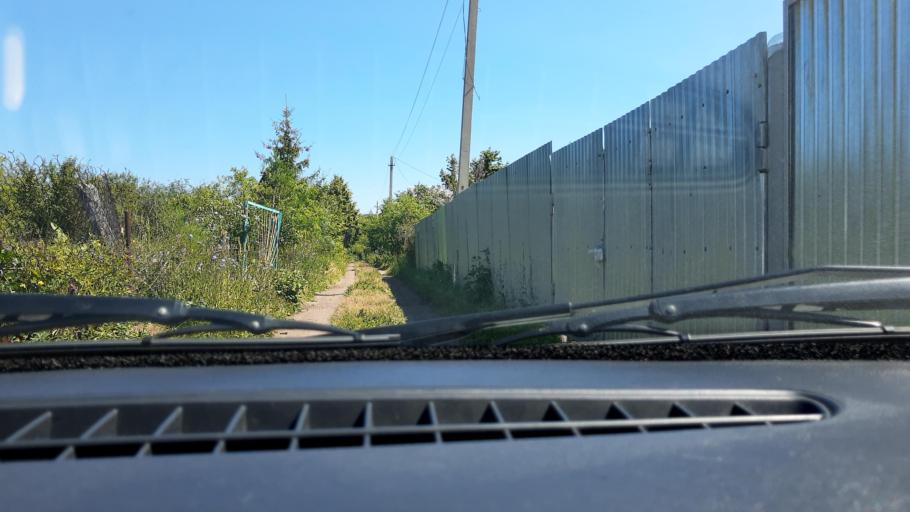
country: RU
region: Bashkortostan
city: Karmaskaly
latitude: 54.3628
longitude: 55.8903
